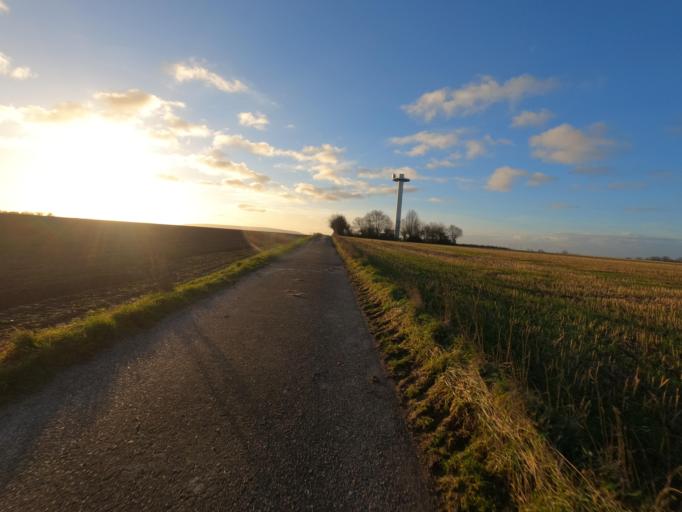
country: DE
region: North Rhine-Westphalia
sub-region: Regierungsbezirk Koln
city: Titz
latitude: 51.0203
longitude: 6.3920
